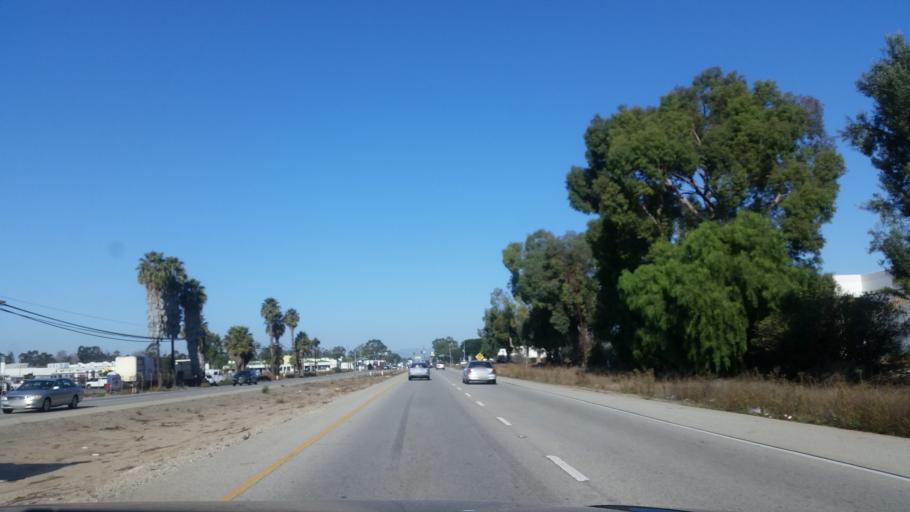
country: US
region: California
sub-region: Ventura County
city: Oxnard
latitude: 34.1777
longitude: -119.1624
